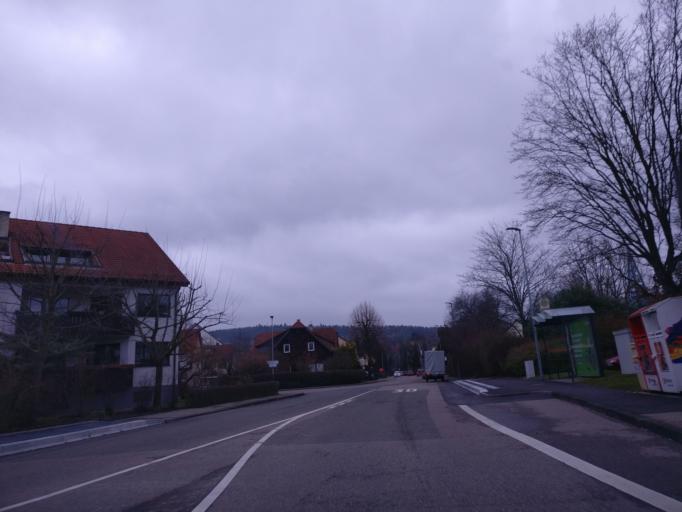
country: DE
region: Baden-Wuerttemberg
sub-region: Regierungsbezirk Stuttgart
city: Schorndorf
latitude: 48.8142
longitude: 9.5277
